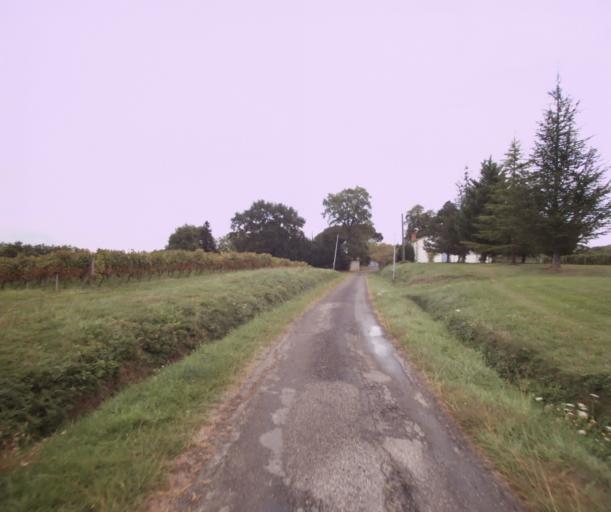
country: FR
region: Midi-Pyrenees
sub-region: Departement du Gers
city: Cazaubon
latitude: 43.8746
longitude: -0.0632
